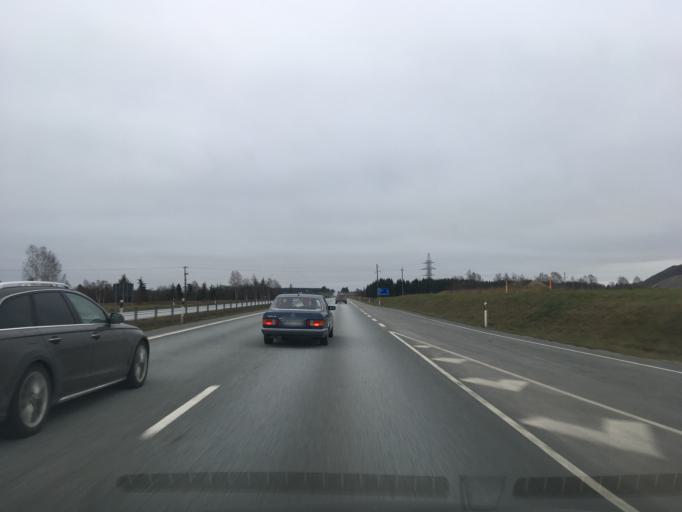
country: EE
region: Laeaene-Virumaa
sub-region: Haljala vald
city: Haljala
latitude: 59.4228
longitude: 26.2793
